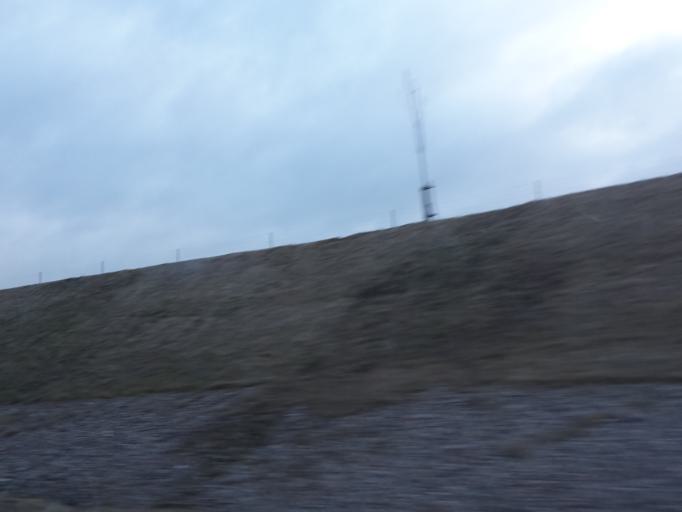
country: PL
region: Warmian-Masurian Voivodeship
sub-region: Powiat ostrodzki
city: Maldyty
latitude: 53.9576
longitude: 19.6969
